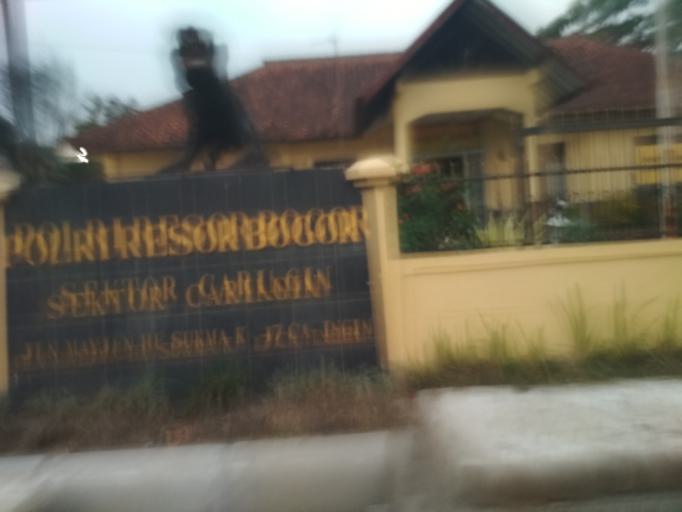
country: ID
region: West Java
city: Caringin
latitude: -6.7096
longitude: 106.8226
